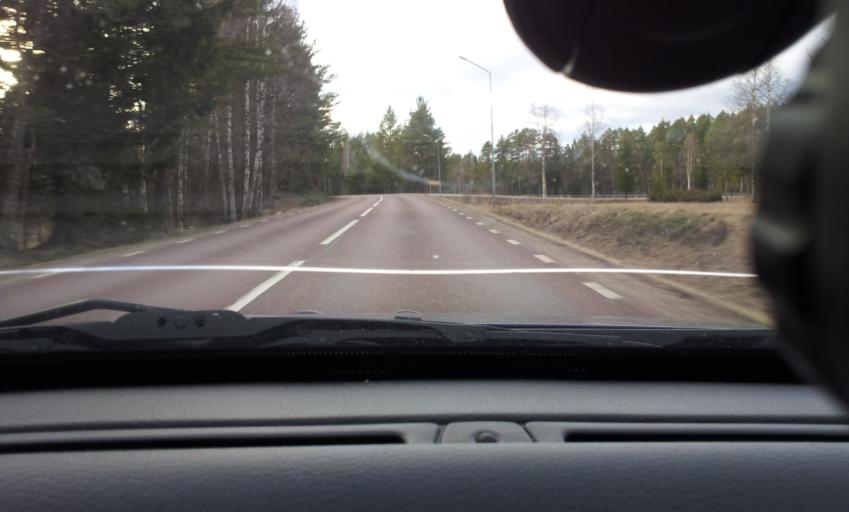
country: SE
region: Jaemtland
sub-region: Harjedalens Kommun
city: Sveg
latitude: 62.1773
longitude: 14.9112
